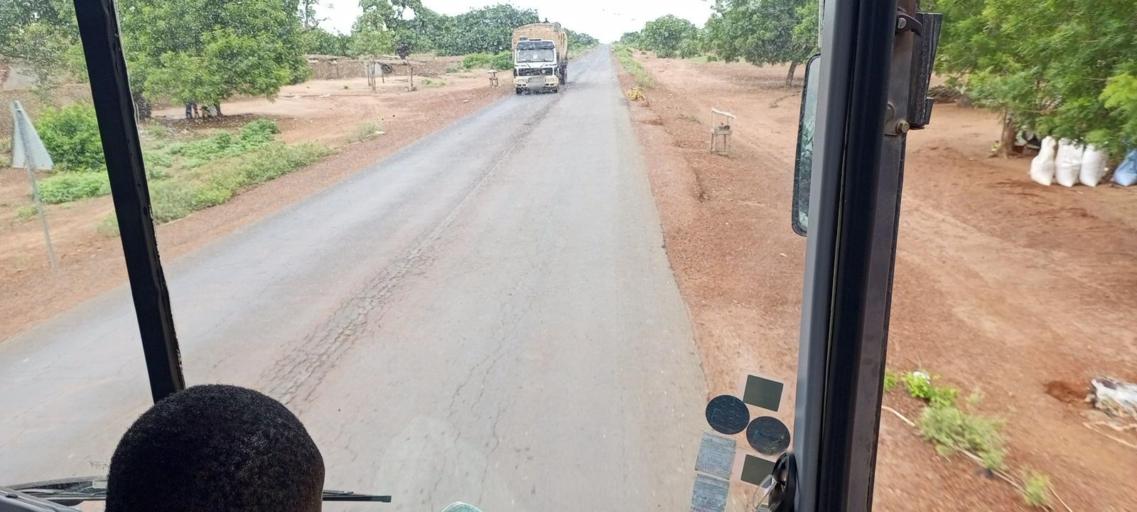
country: ML
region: Sikasso
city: Koutiala
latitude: 12.5774
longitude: -5.6079
